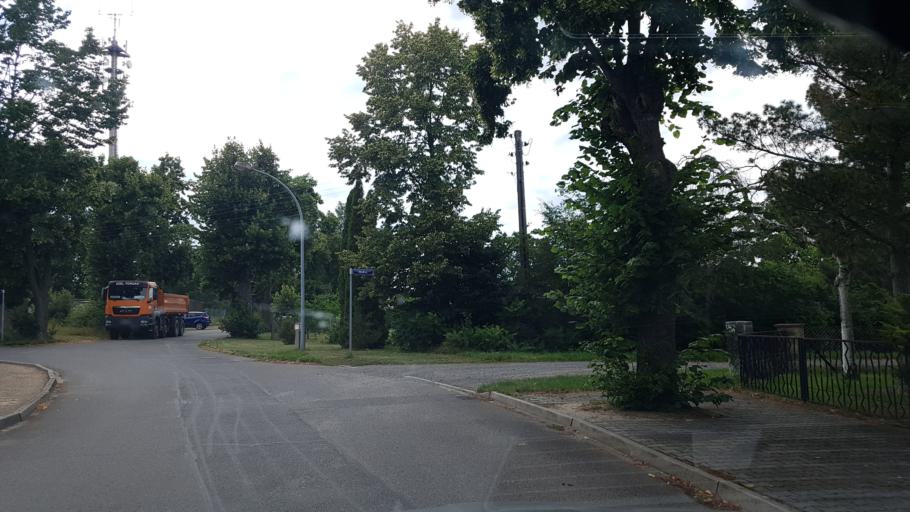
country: DE
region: Brandenburg
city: Falkenberg
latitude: 51.5824
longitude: 13.2279
